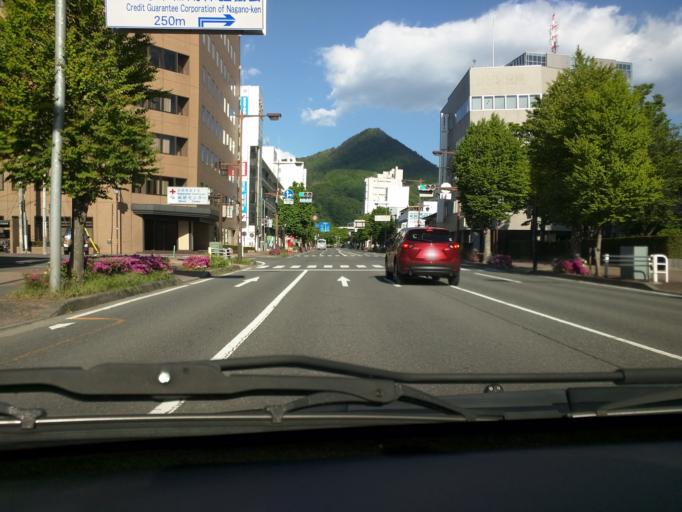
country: JP
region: Nagano
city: Nagano-shi
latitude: 36.6496
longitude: 138.1852
